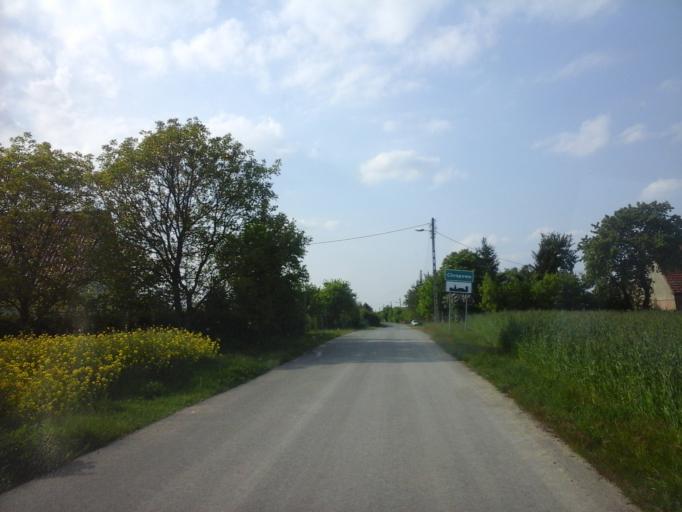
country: PL
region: West Pomeranian Voivodeship
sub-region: Powiat choszczenski
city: Pelczyce
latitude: 53.0402
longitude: 15.2559
